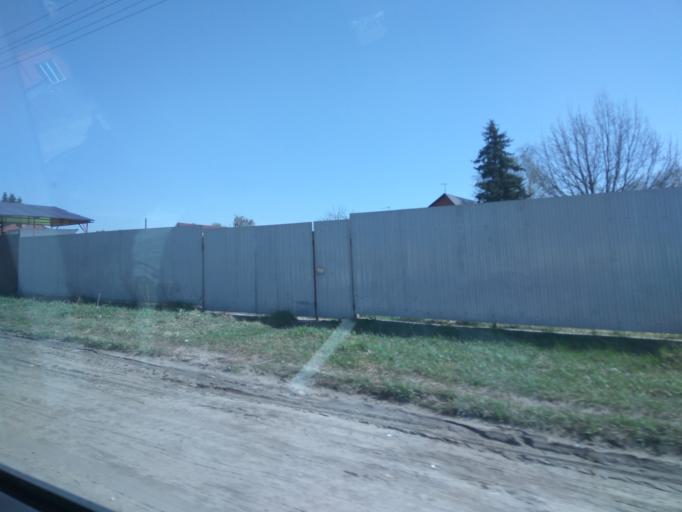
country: RU
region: Moskovskaya
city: Ramenskoye
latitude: 55.5504
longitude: 38.2343
